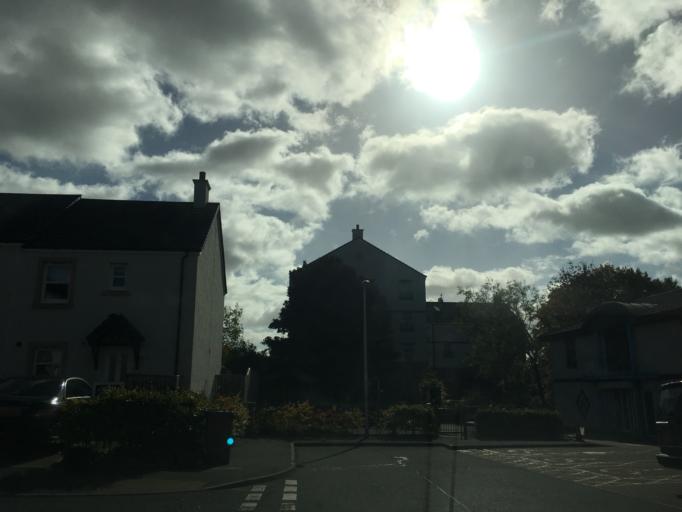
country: GB
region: Scotland
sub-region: Edinburgh
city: Currie
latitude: 55.9510
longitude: -3.3035
